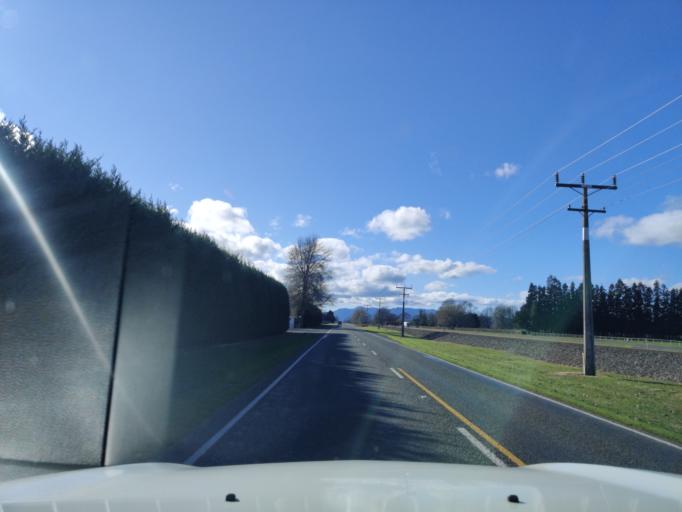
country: NZ
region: Waikato
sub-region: Matamata-Piako District
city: Matamata
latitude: -37.8506
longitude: 175.7593
